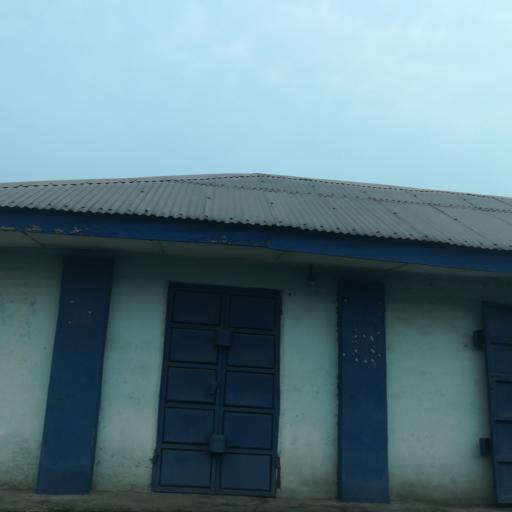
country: NG
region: Rivers
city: Port Harcourt
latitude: 4.7655
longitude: 7.0105
